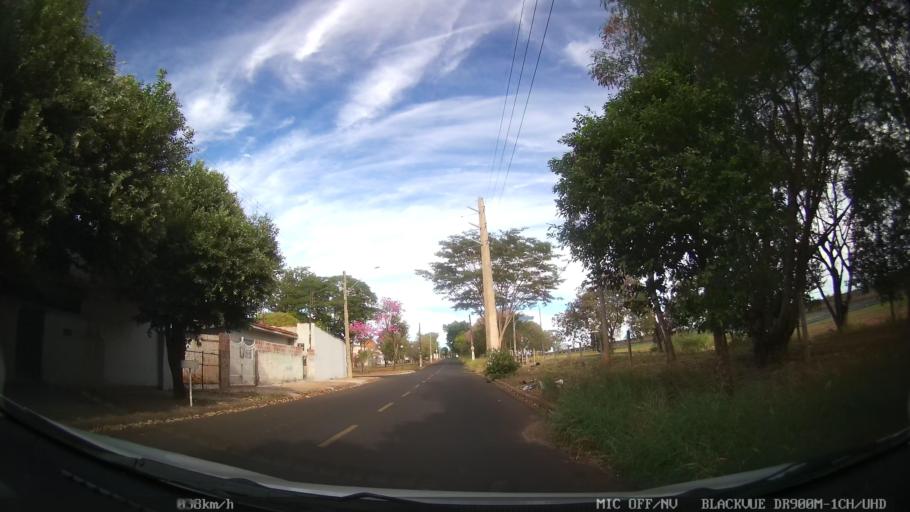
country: BR
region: Sao Paulo
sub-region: Catanduva
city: Catanduva
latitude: -21.1240
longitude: -48.9967
